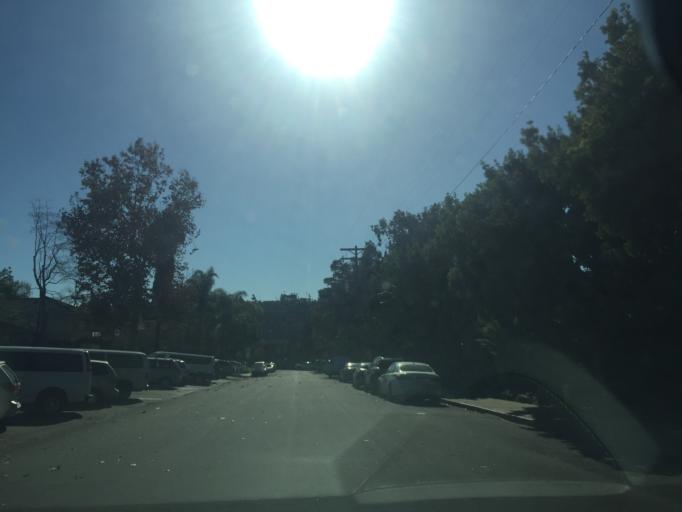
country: US
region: California
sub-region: San Diego County
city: La Mesa
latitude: 32.7862
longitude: -117.0968
